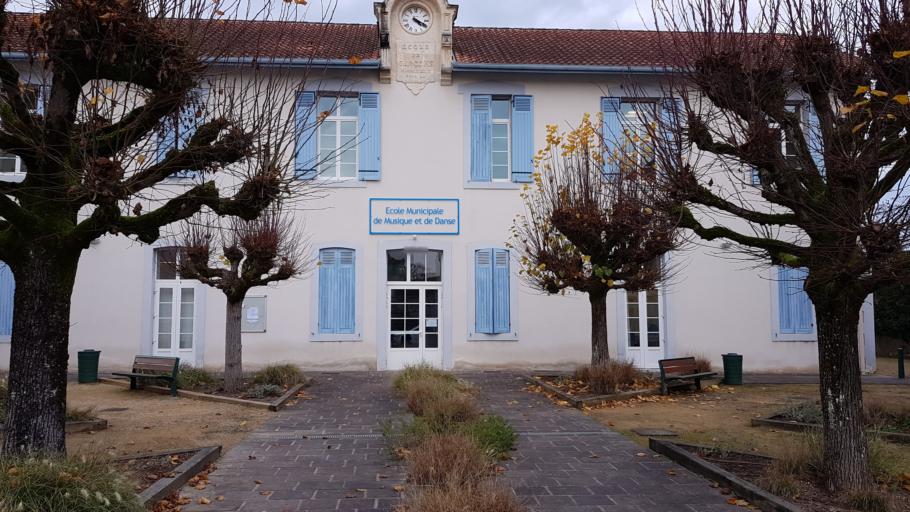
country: FR
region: Aquitaine
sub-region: Departement des Landes
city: Saint-Paul-les-Dax
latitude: 43.7241
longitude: -1.0539
